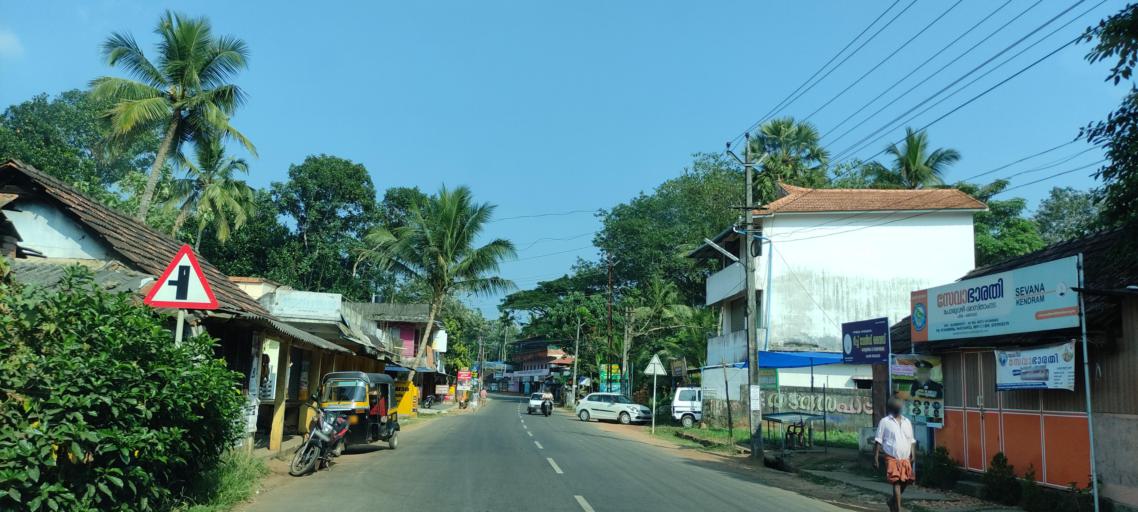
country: IN
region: Kerala
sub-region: Pattanamtitta
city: Adur
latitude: 9.0742
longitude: 76.6590
